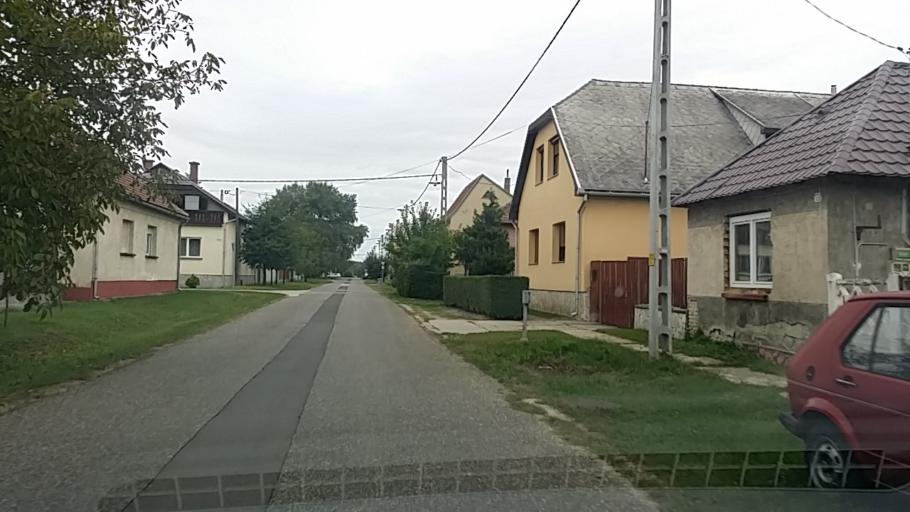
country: HU
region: Komarom-Esztergom
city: Tat
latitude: 47.7397
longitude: 18.6647
